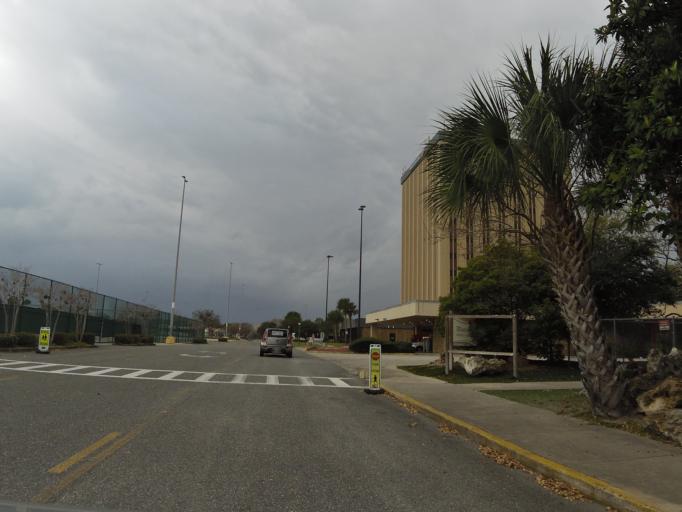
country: US
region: Florida
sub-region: Duval County
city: Jacksonville
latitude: 30.3252
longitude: -81.5489
